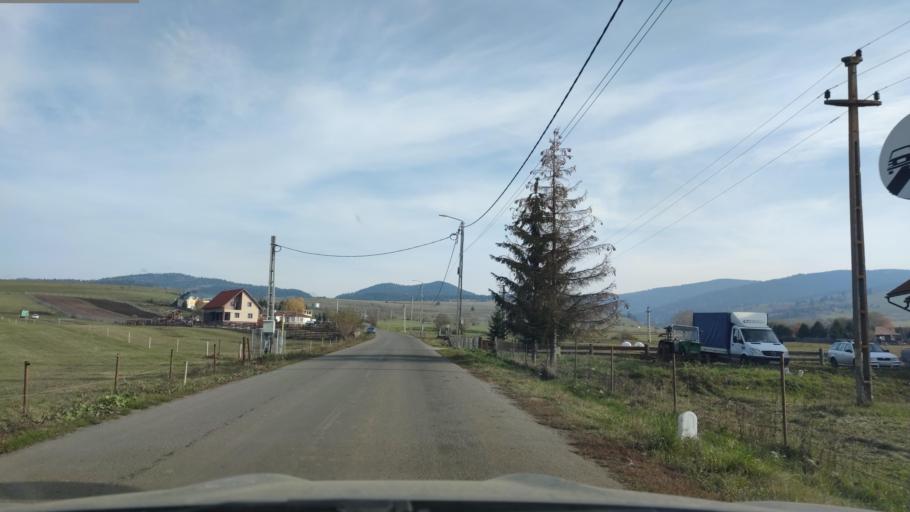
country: RO
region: Harghita
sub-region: Comuna Ditrau
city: Ditrau
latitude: 46.8205
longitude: 25.5292
